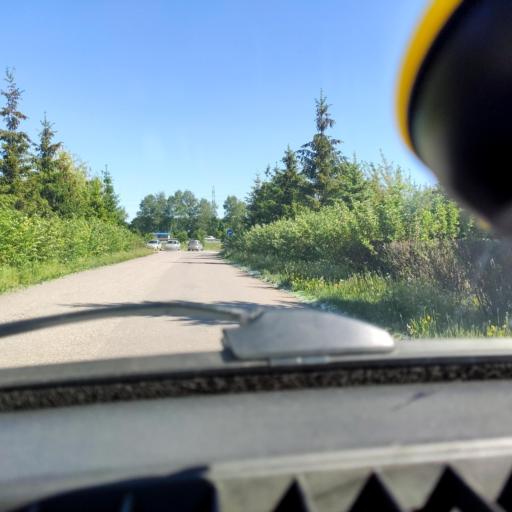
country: RU
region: Samara
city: Tol'yatti
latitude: 53.5760
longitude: 49.4252
